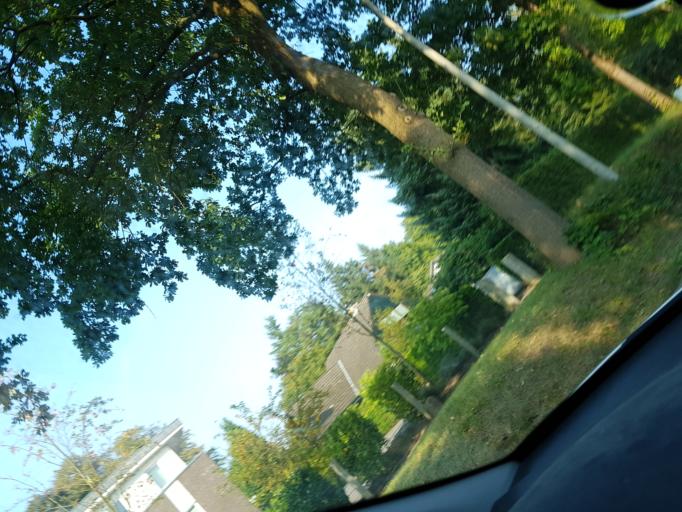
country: DE
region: Hamburg
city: Wellingsbuettel
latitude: 53.6400
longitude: 10.0861
